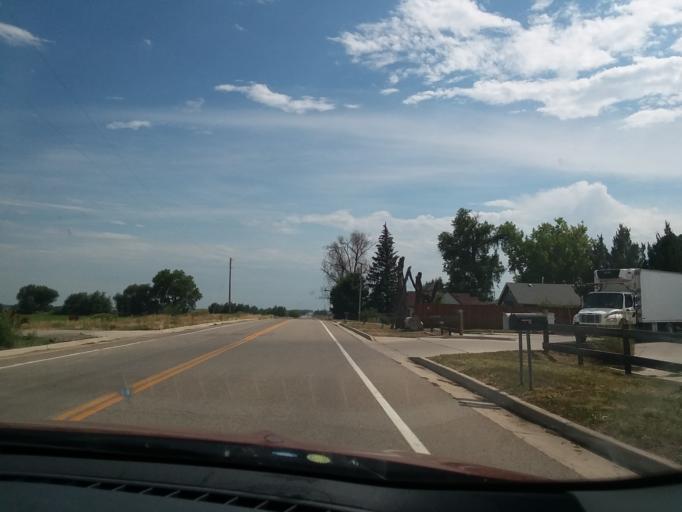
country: US
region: Colorado
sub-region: Larimer County
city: Berthoud
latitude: 40.3046
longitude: -105.1028
